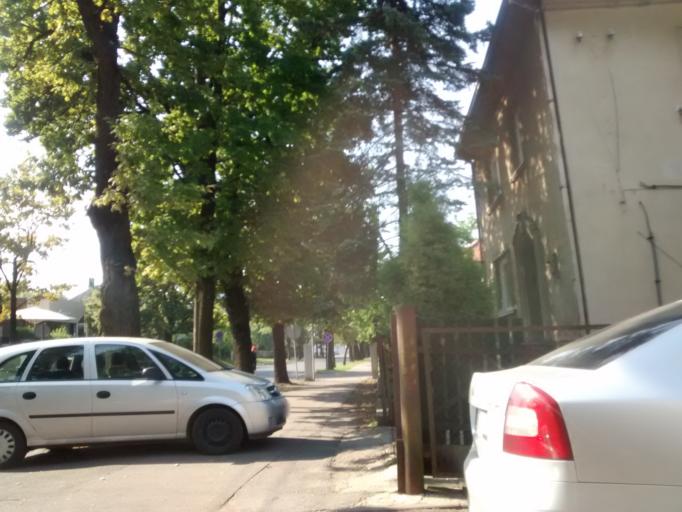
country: LT
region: Kauno apskritis
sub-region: Kaunas
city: Eiguliai
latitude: 54.9166
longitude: 23.9207
